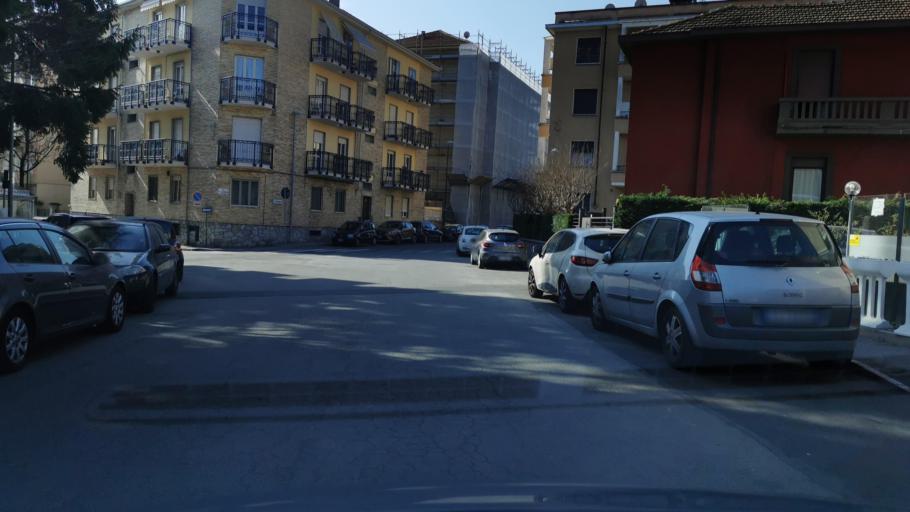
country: IT
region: Piedmont
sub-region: Provincia di Torino
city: Pinerolo
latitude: 44.8915
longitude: 7.3329
